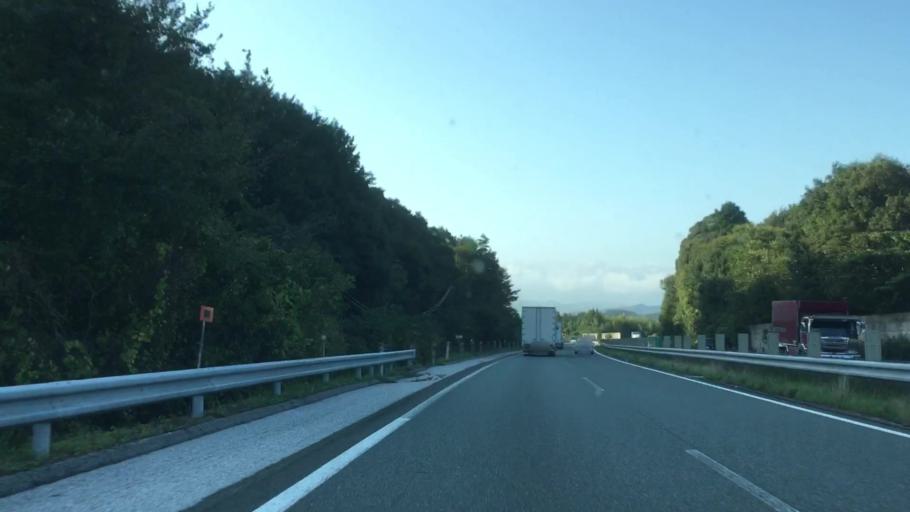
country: JP
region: Yamaguchi
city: Ogori-shimogo
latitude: 34.1484
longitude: 131.3433
